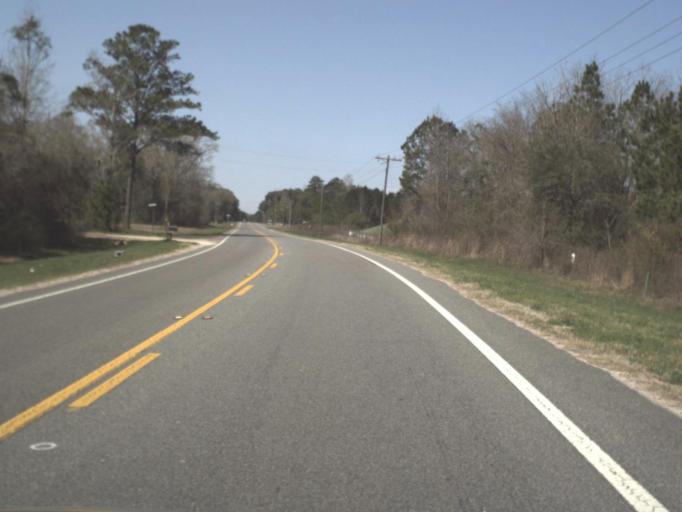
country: US
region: Florida
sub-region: Gadsden County
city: Quincy
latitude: 30.5920
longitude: -84.5083
